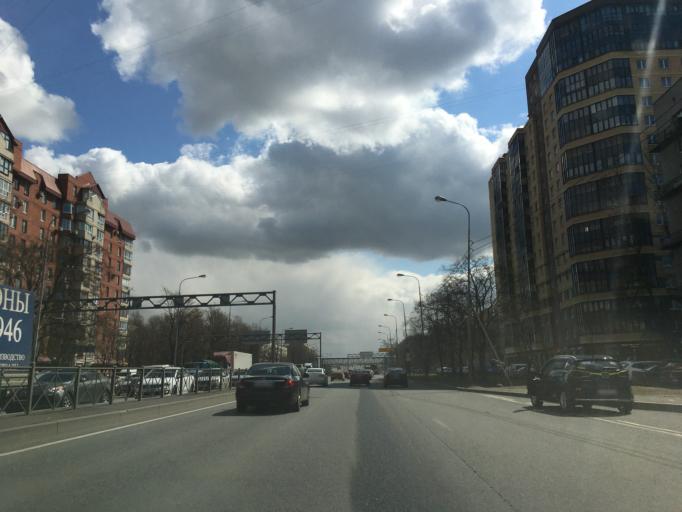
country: RU
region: St.-Petersburg
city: Dachnoye
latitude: 59.8410
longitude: 30.2564
